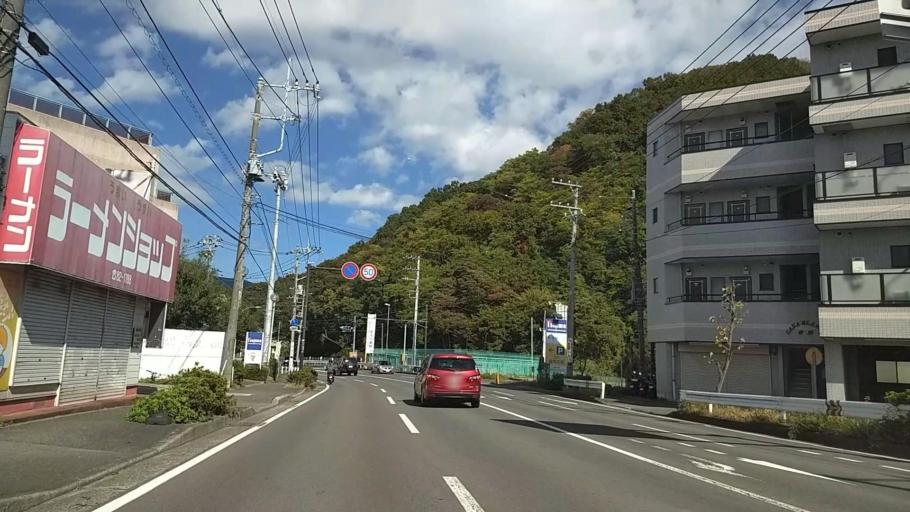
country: JP
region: Kanagawa
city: Hadano
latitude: 35.3699
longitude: 139.2359
